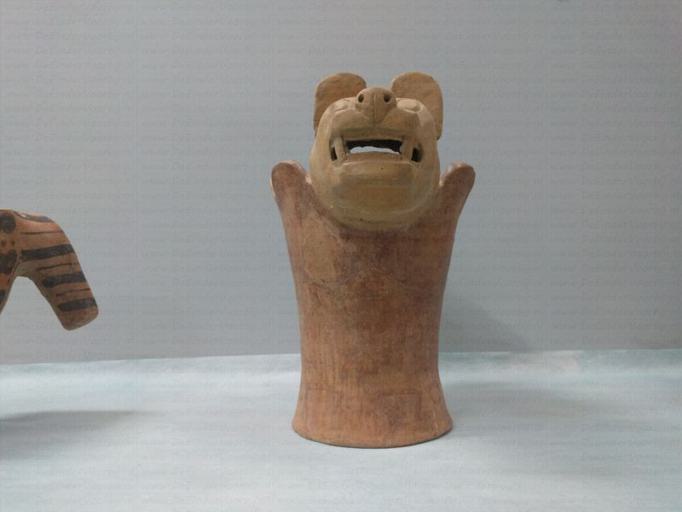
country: BO
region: La Paz
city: Tiahuanaco
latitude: -16.5580
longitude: -68.6760
